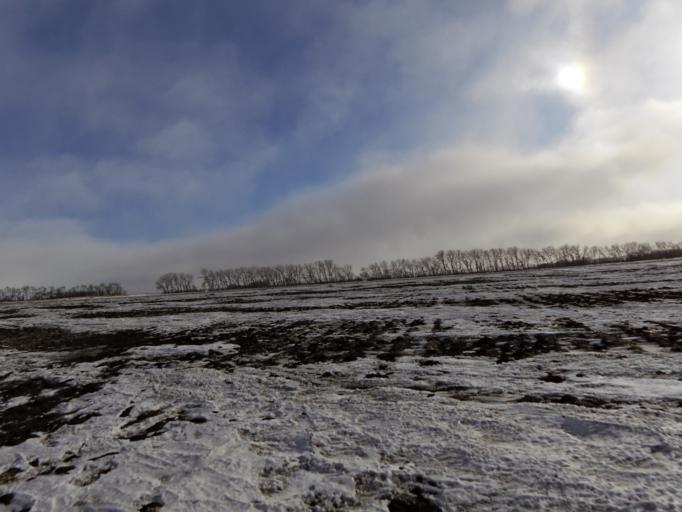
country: US
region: North Dakota
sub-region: Walsh County
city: Grafton
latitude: 48.3984
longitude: -97.2037
